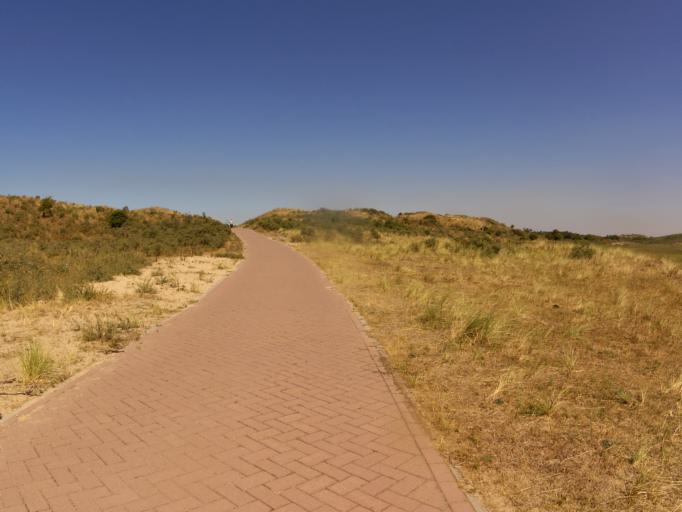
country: NL
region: North Holland
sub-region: Gemeente Bloemendaal
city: Bloemendaal
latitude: 52.4227
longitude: 4.5694
